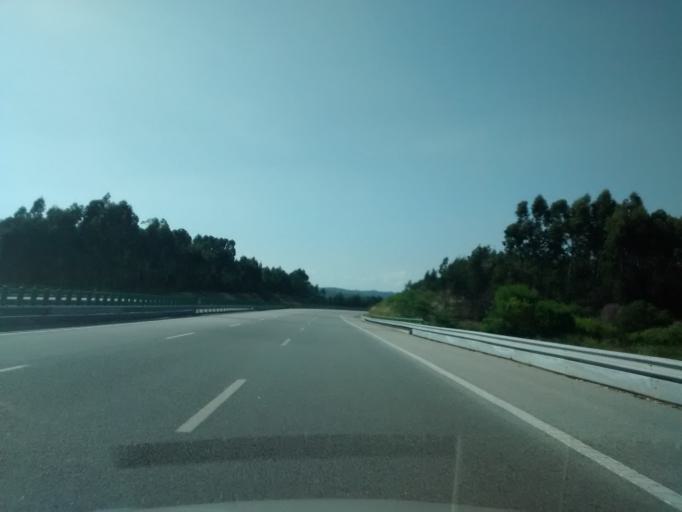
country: PT
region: Coimbra
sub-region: Montemor-O-Velho
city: Montemor-o-Velho
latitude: 40.1140
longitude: -8.7458
